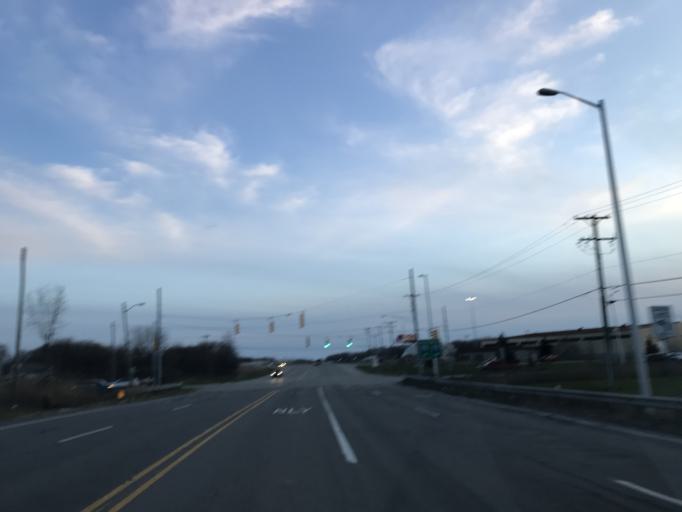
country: US
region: Michigan
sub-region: Wayne County
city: Woodhaven
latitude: 42.1708
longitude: -83.2394
